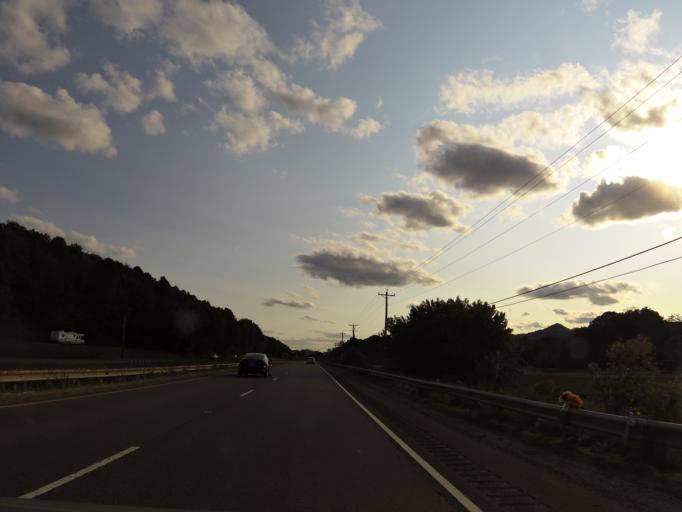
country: US
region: Virginia
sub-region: Russell County
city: Honaker
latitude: 36.9631
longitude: -81.9242
